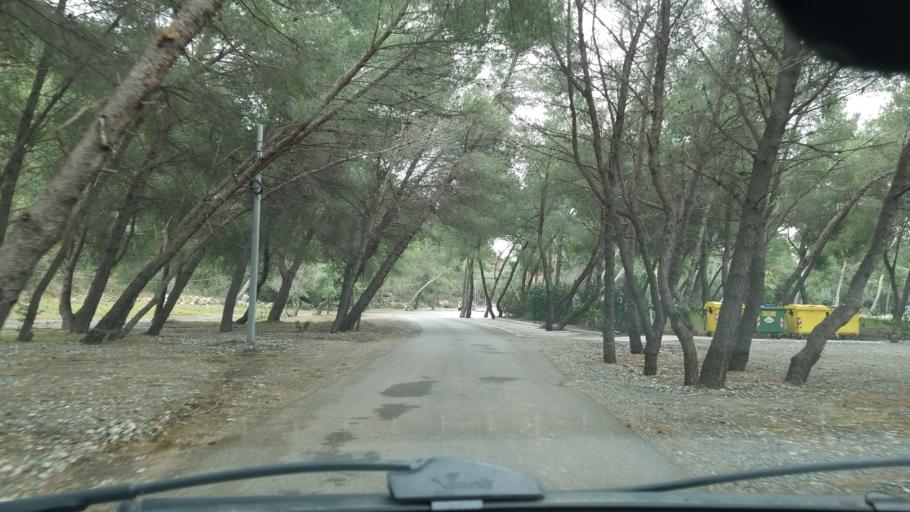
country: AL
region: Lezhe
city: Shengjin
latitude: 41.8230
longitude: 19.5610
